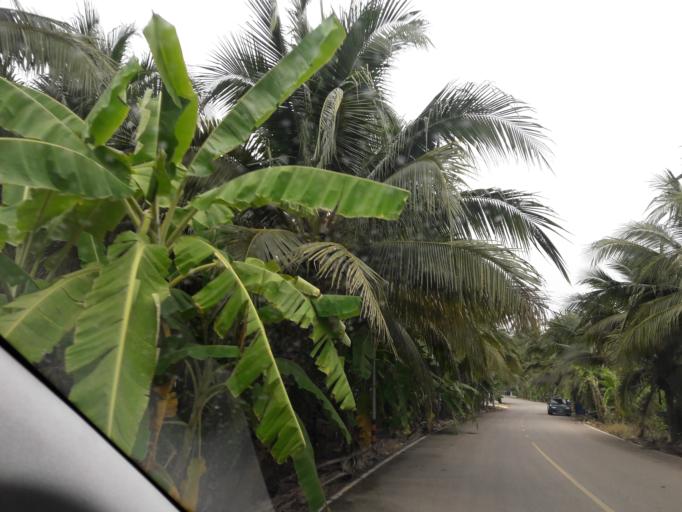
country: TH
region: Ratchaburi
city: Damnoen Saduak
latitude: 13.5242
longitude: 99.9496
